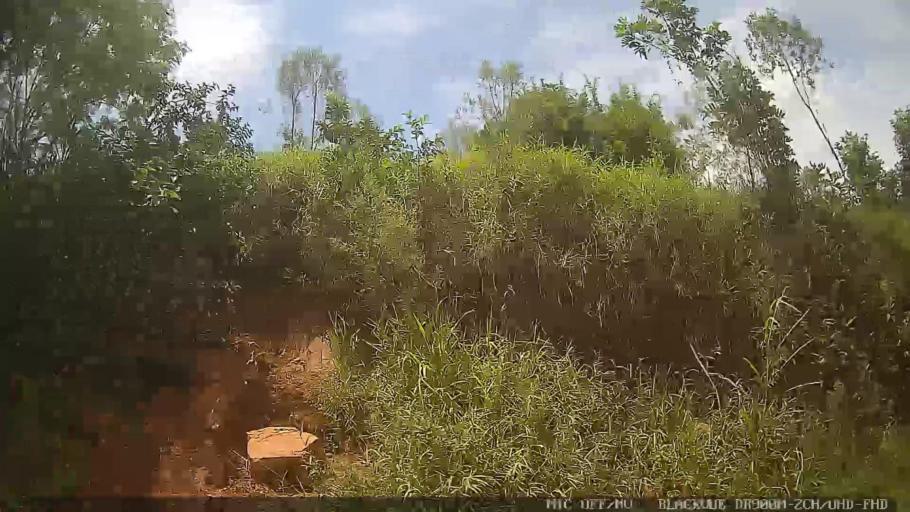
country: BR
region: Sao Paulo
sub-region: Santa Isabel
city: Santa Isabel
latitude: -23.3453
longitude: -46.1863
